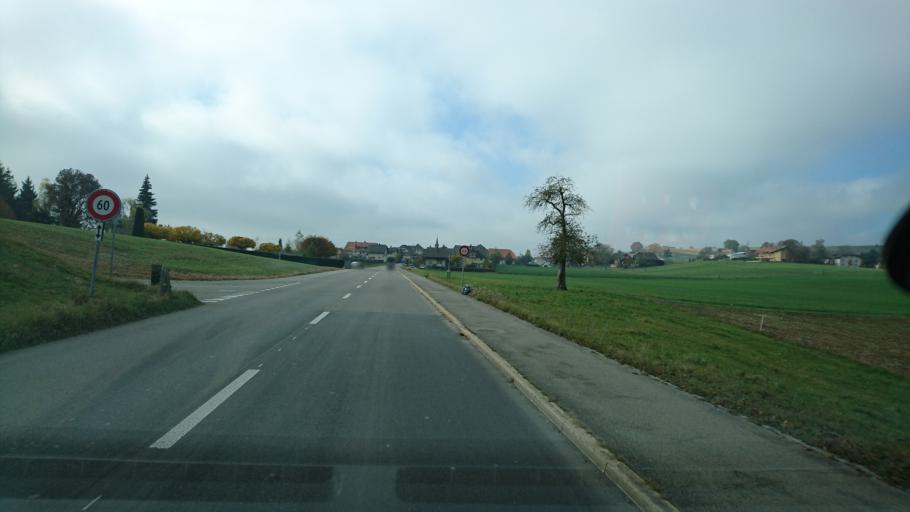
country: CH
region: Bern
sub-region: Bern-Mittelland District
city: Kirchlindach
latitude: 47.0017
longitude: 7.4216
